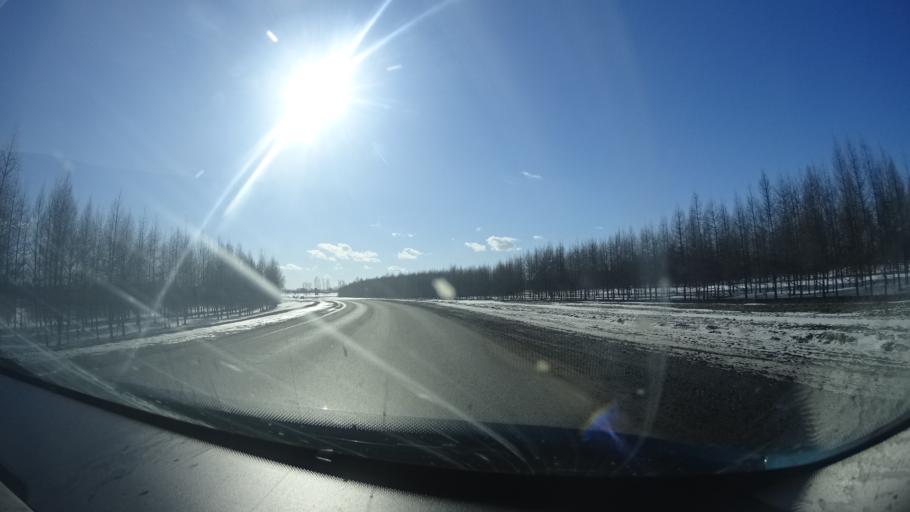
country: RU
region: Bashkortostan
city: Chishmy
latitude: 54.5785
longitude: 55.3642
